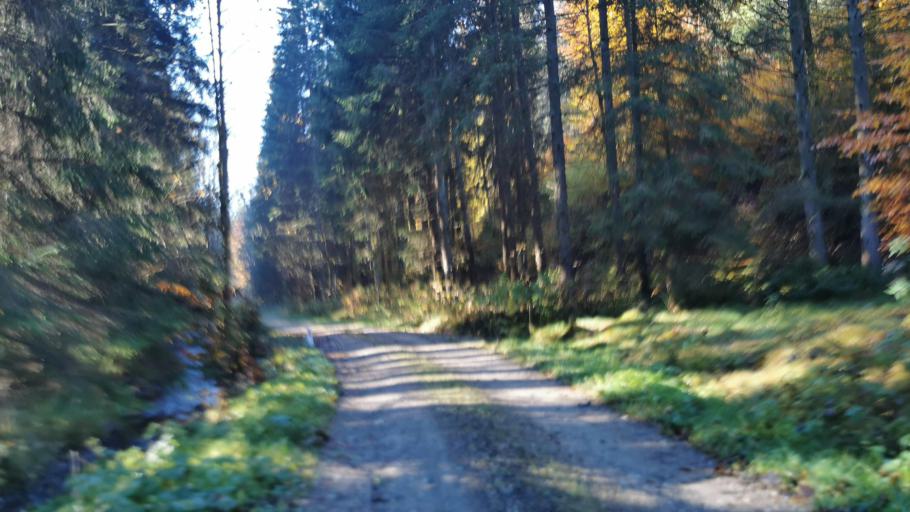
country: DE
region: Bavaria
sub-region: Upper Franconia
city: Nordhalben
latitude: 50.3948
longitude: 11.5347
